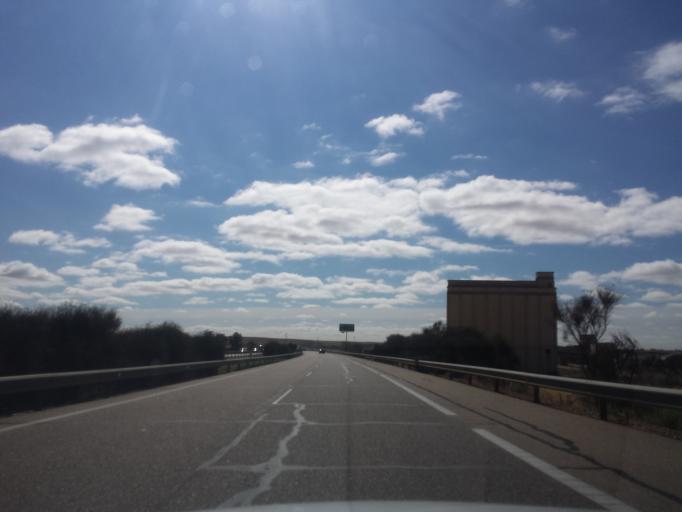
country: ES
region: Castille and Leon
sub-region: Provincia de Zamora
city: Cerecinos de Campos
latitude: 41.9056
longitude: -5.4918
